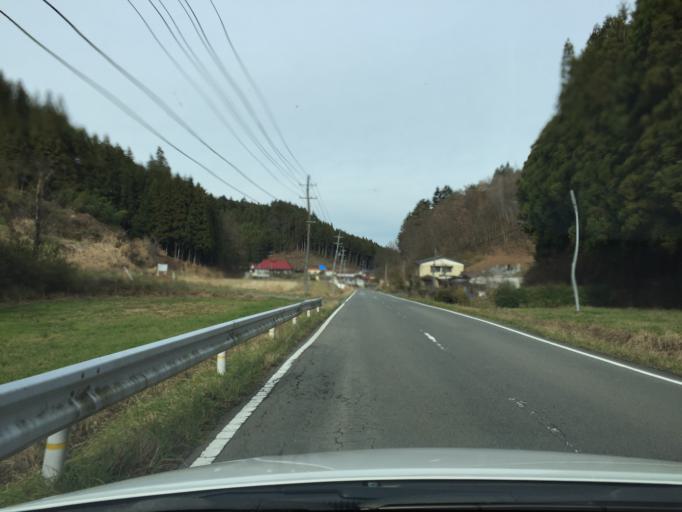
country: JP
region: Fukushima
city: Ishikawa
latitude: 37.2029
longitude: 140.6271
